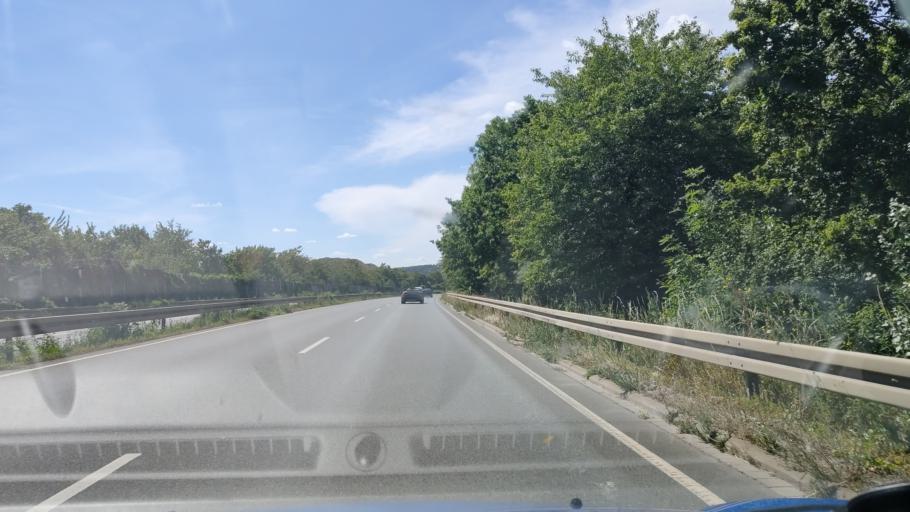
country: DE
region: Lower Saxony
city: Ronnenberg
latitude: 52.3477
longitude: 9.6677
